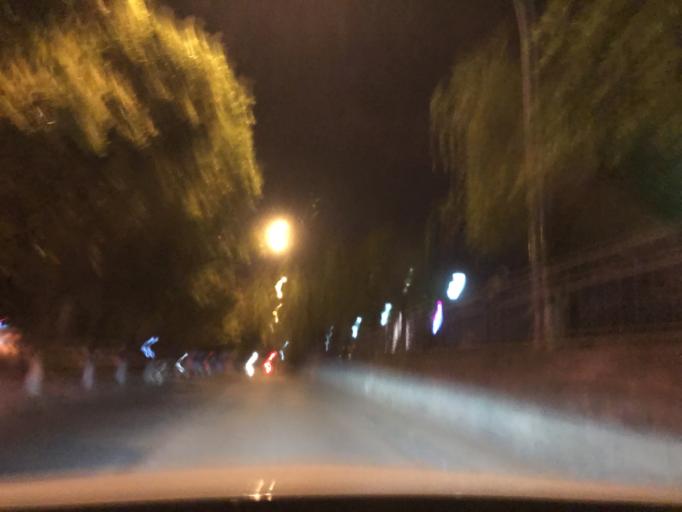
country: CN
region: Sichuan
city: Mianyang
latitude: 31.4536
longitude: 104.7470
